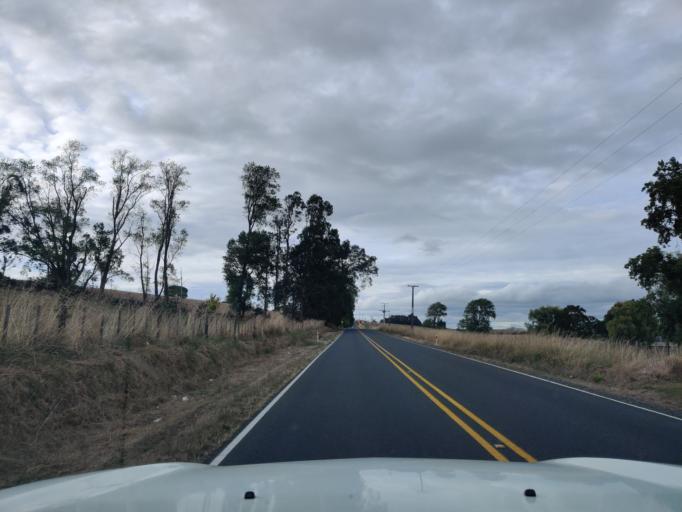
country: NZ
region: Waikato
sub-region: Waipa District
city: Cambridge
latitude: -37.8032
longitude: 175.4490
